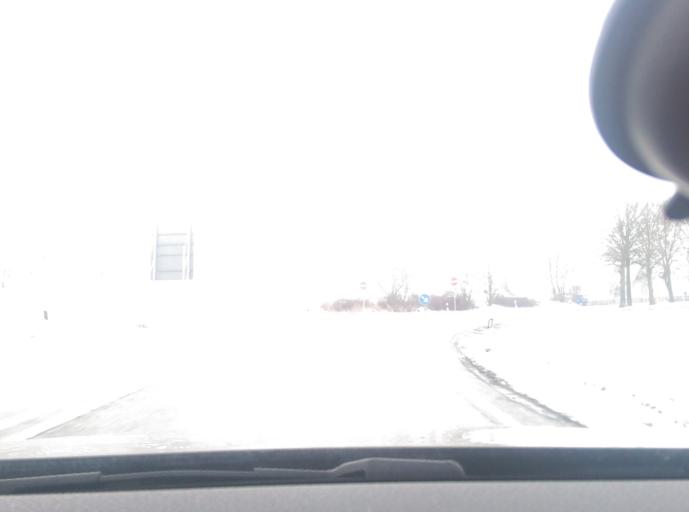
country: DE
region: Hesse
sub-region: Regierungsbezirk Kassel
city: Baunatal
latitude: 51.2570
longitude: 9.4456
